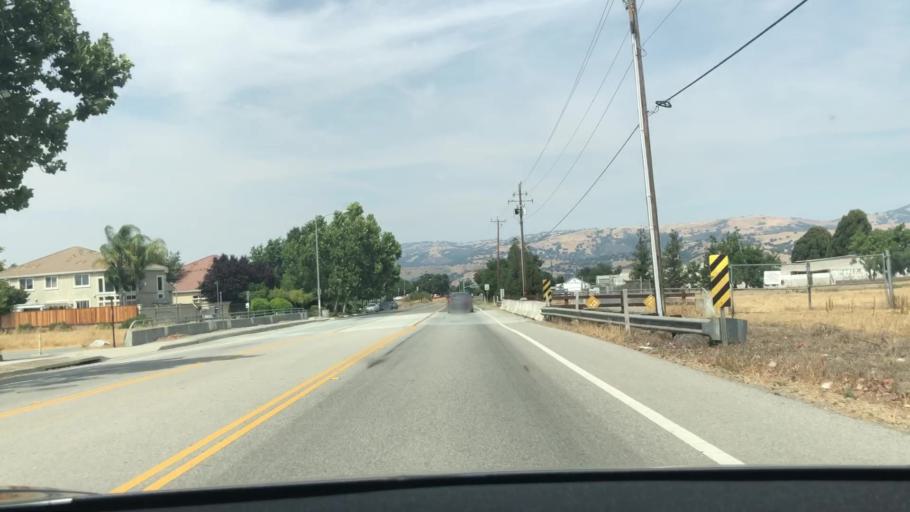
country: US
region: California
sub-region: Santa Clara County
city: Morgan Hill
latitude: 37.1044
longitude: -121.6384
